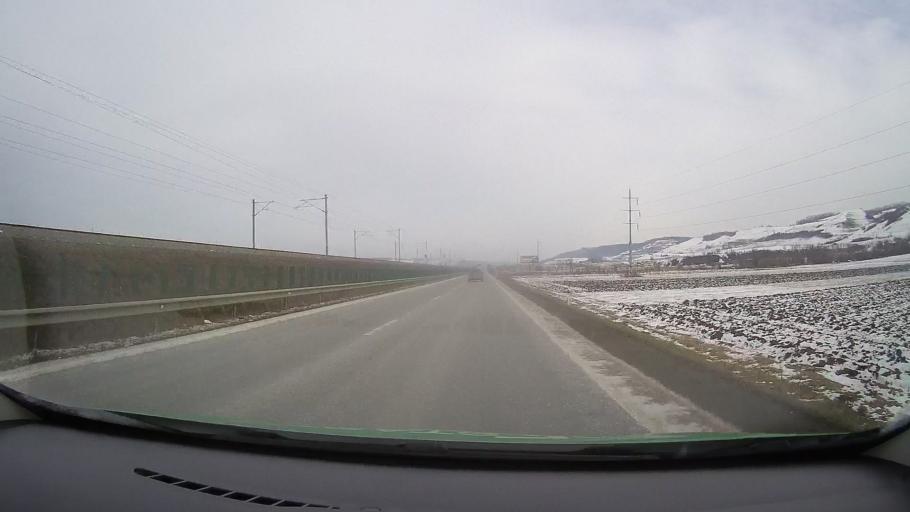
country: RO
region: Sibiu
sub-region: Comuna Brateiu
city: Brateiu
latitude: 46.1826
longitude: 24.4414
